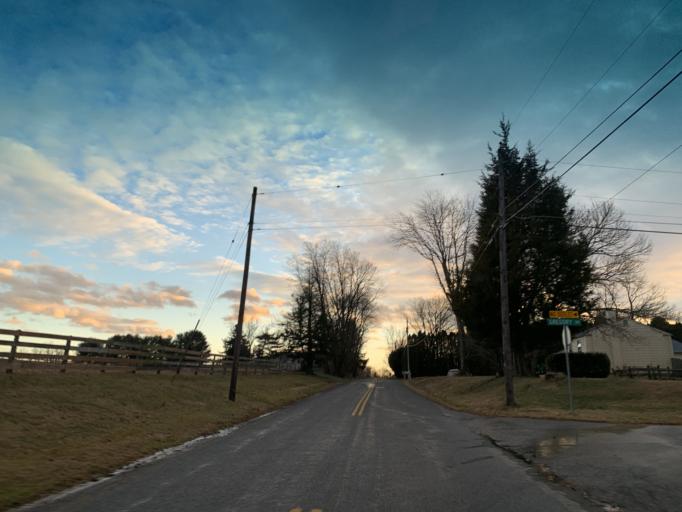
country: US
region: Maryland
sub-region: Harford County
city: South Bel Air
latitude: 39.5992
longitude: -76.3204
